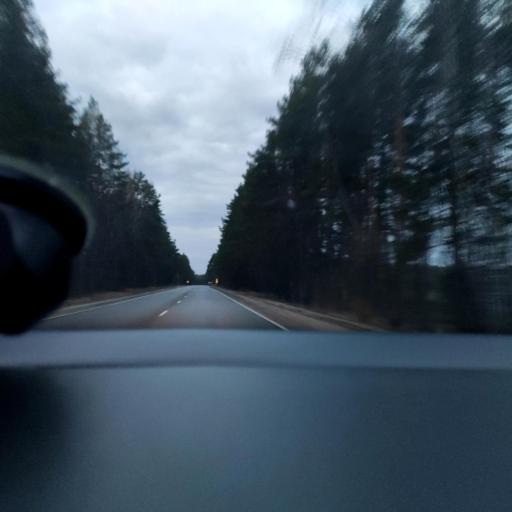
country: RU
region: Moskovskaya
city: Krasnyy Tkach
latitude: 55.4170
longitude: 39.1782
